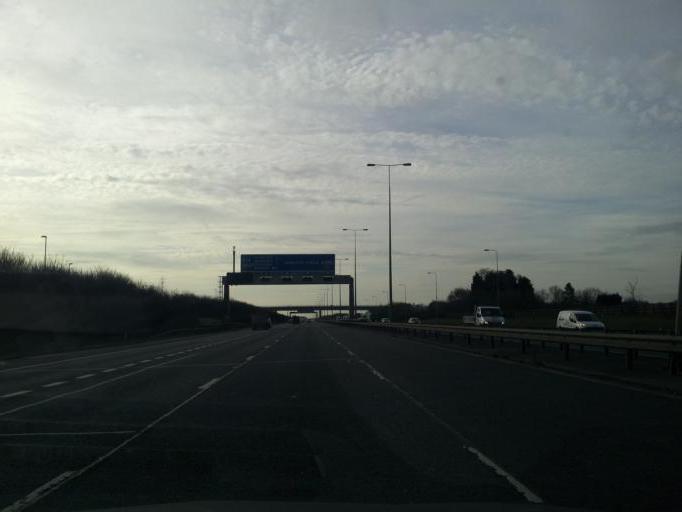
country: GB
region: England
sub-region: Cambridgeshire
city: Sawtry
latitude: 52.3896
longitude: -0.2591
